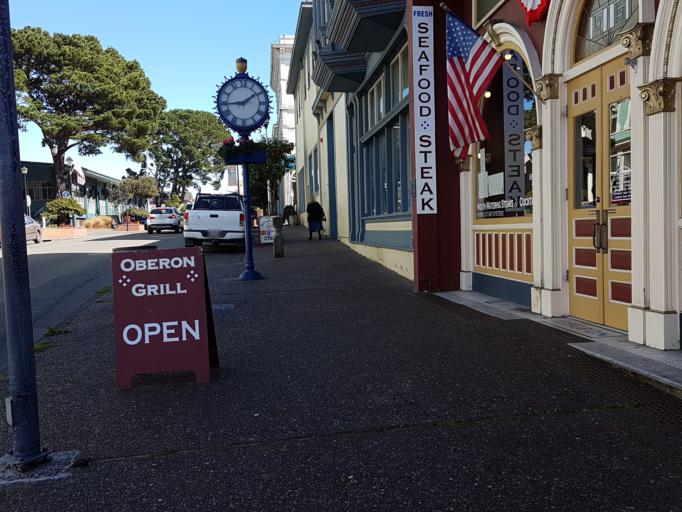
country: US
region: California
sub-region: Humboldt County
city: Eureka
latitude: 40.8044
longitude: -124.1662
